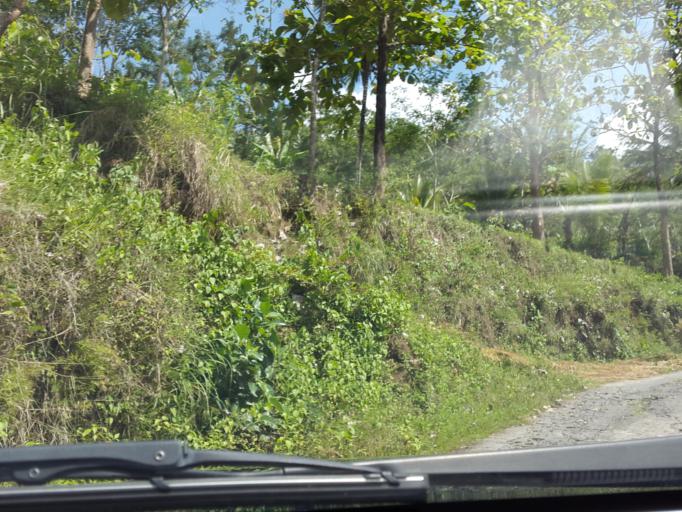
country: ID
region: Central Java
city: Selogiri
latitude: -7.8950
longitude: 110.7540
